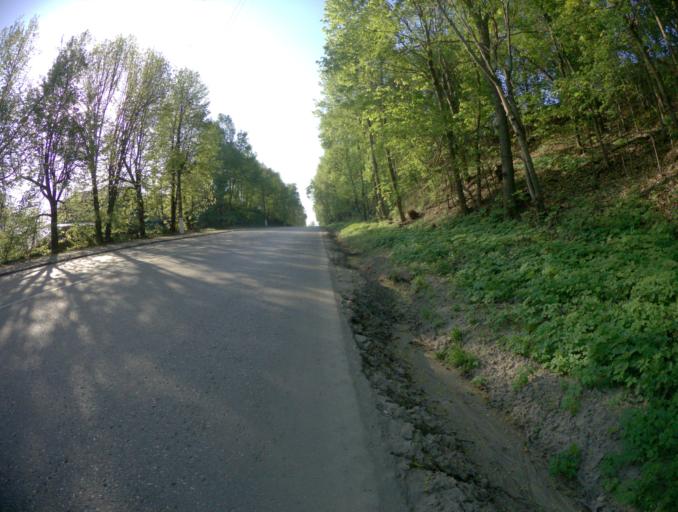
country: RU
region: Vladimir
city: Vyazniki
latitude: 56.2417
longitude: 42.1682
